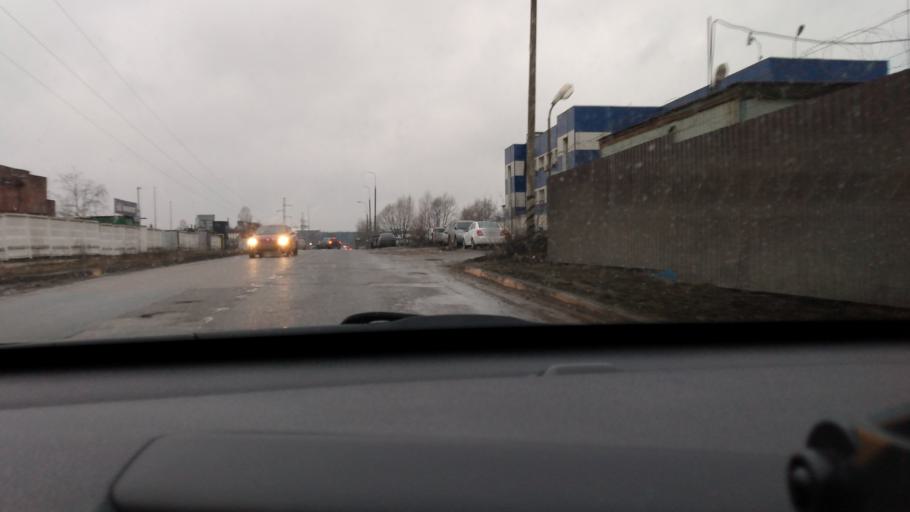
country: RU
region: Moskovskaya
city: Odintsovo
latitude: 55.6718
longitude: 37.2442
